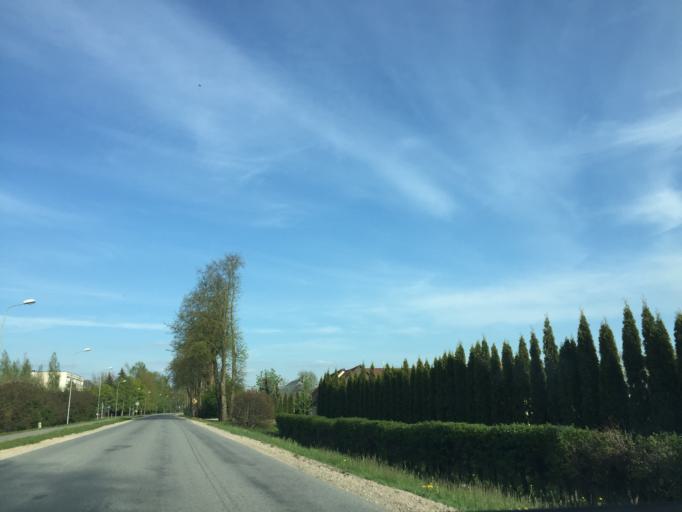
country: LV
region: Bauskas Rajons
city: Bauska
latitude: 56.3984
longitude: 24.1900
